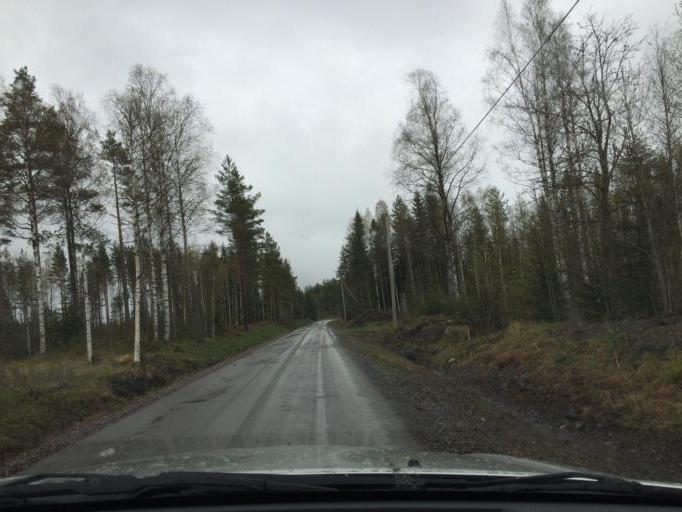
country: SE
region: Dalarna
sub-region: Ludvika Kommun
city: Abborrberget
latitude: 60.0413
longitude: 14.7002
